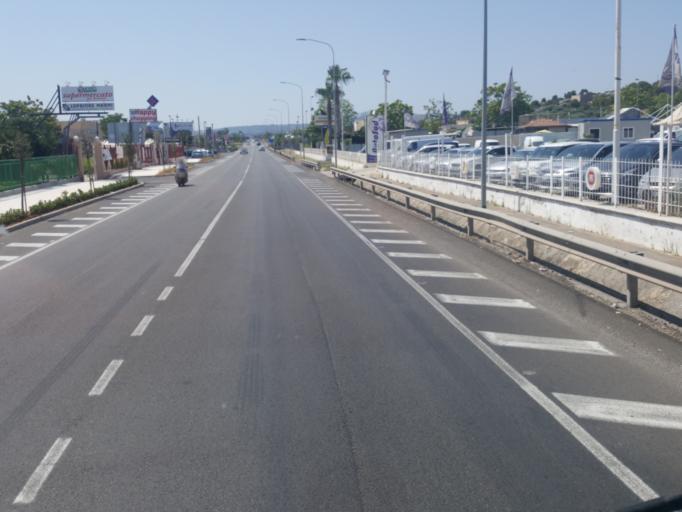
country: IT
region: Apulia
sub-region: Provincia di Taranto
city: Massafra
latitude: 40.5864
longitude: 17.1071
